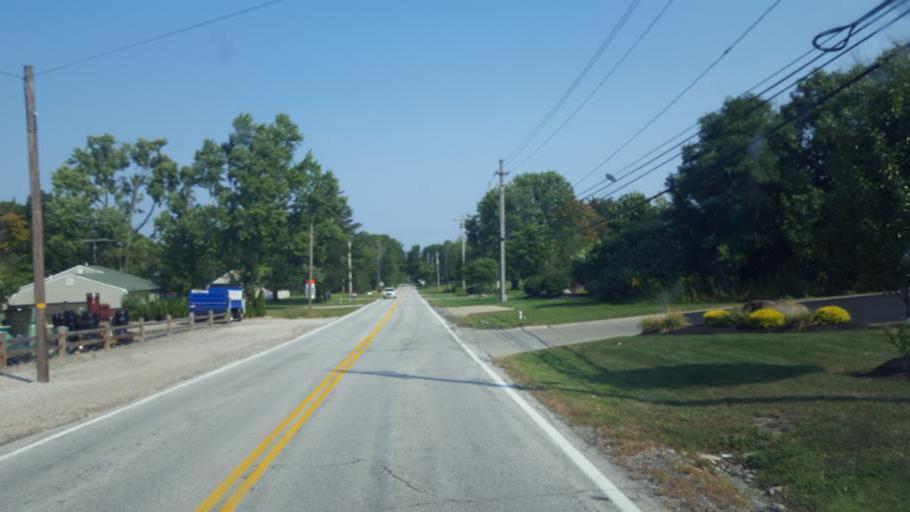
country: US
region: Ohio
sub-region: Lake County
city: Painesville
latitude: 41.6547
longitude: -81.2192
